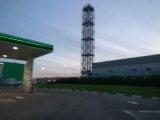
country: RU
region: Moscow
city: Strogino
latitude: 55.8125
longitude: 37.3872
